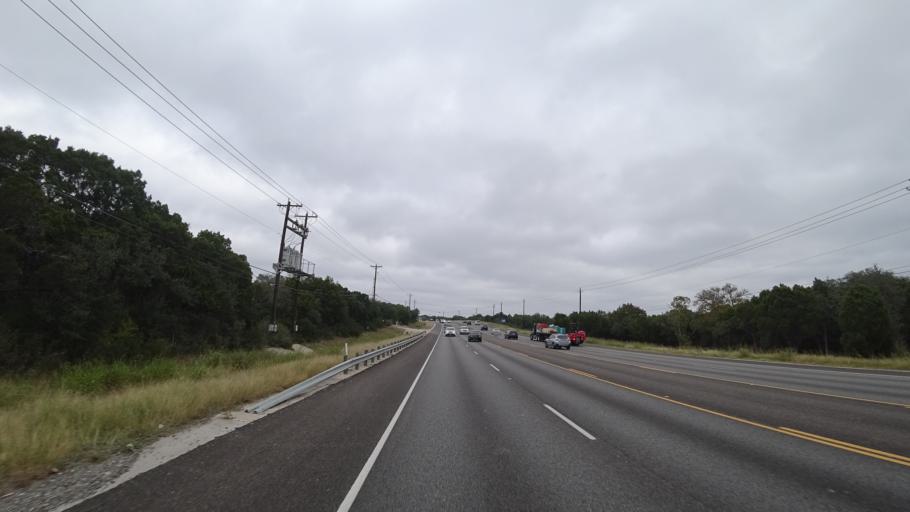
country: US
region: Texas
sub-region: Travis County
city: Bee Cave
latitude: 30.2839
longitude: -97.9168
